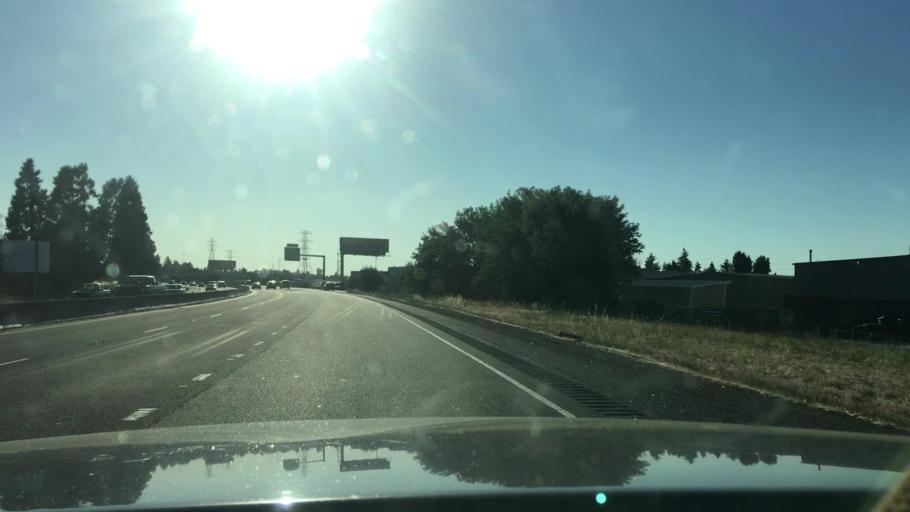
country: US
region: Oregon
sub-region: Lane County
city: Springfield
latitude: 44.0627
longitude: -123.0321
